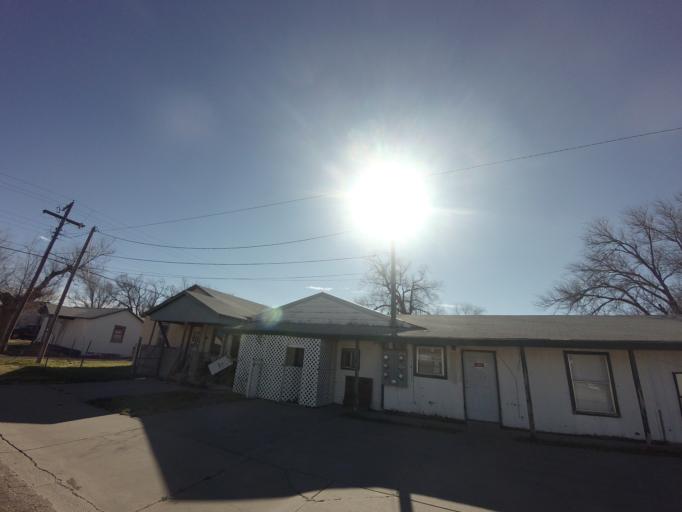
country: US
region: New Mexico
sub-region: Curry County
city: Clovis
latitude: 34.4078
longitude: -103.2138
